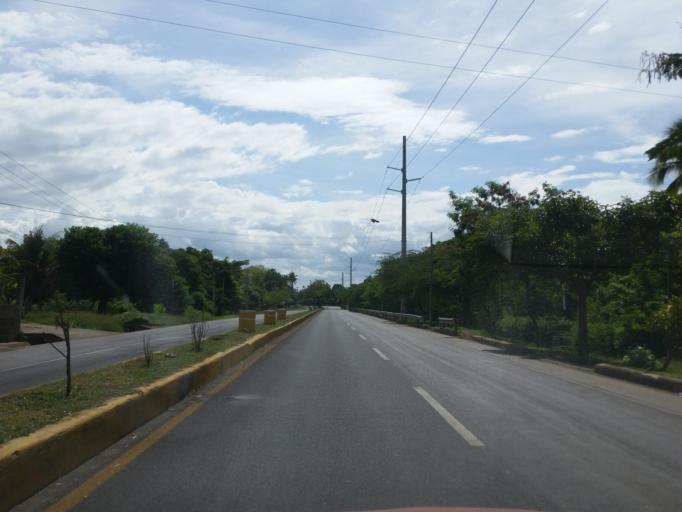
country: NI
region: Masaya
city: Masaya
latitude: 11.9745
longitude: -86.0306
